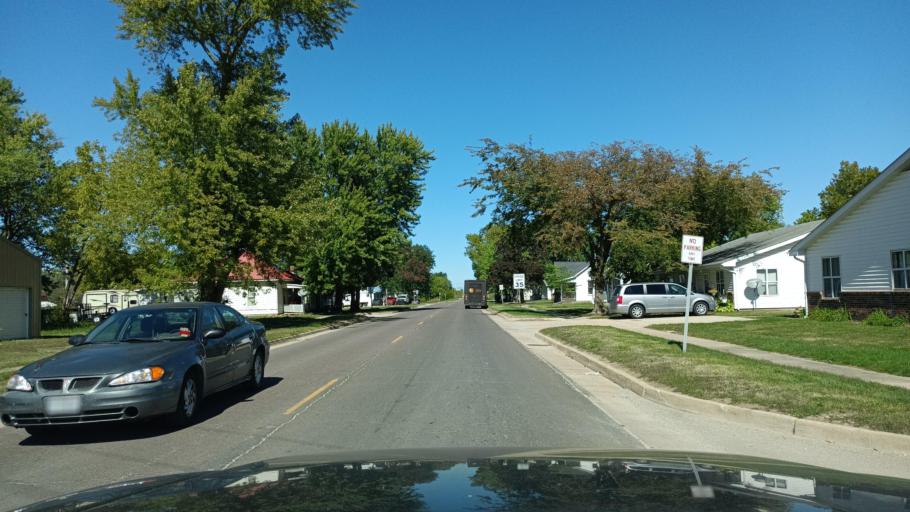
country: US
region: Missouri
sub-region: Macon County
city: La Plata
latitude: 40.0264
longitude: -92.4885
